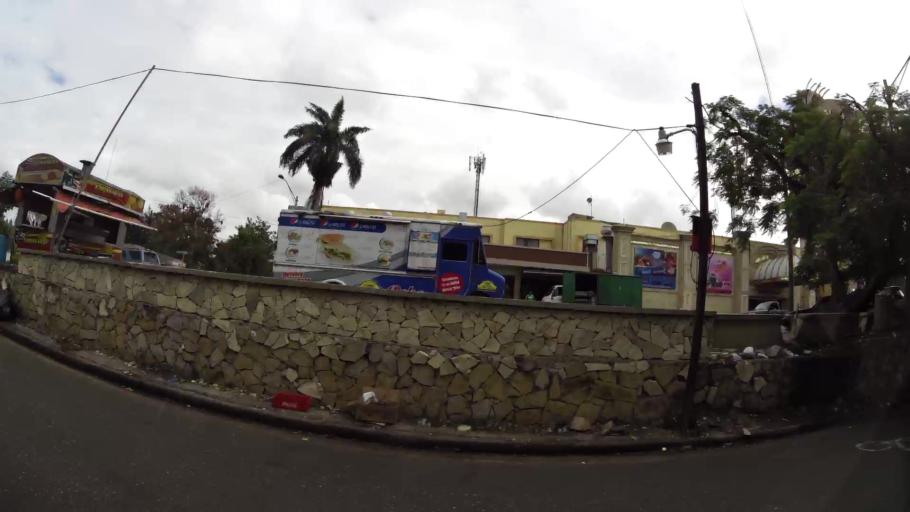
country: DO
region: Santiago
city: Santiago de los Caballeros
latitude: 19.4516
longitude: -70.6916
